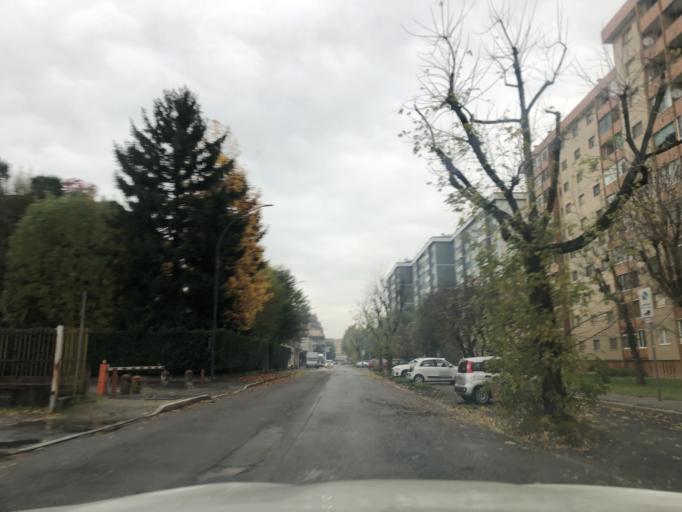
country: IT
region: Lombardy
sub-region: Citta metropolitana di Milano
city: Cesano Boscone
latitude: 45.4356
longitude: 9.0934
